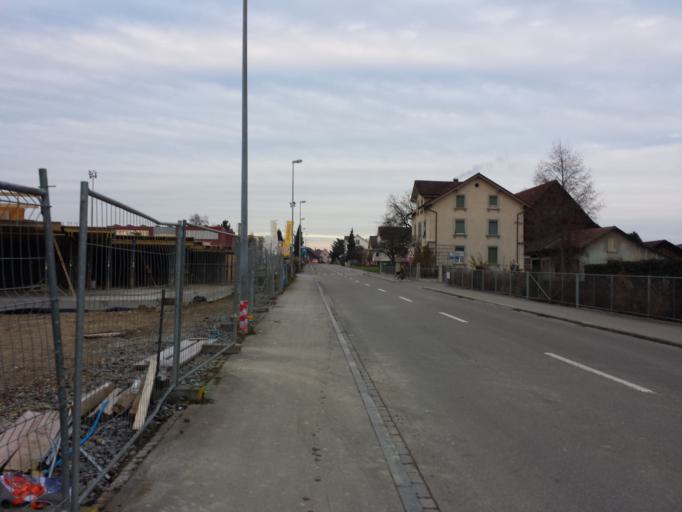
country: CH
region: Thurgau
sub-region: Arbon District
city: Romanshorn
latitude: 47.5705
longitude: 9.3742
